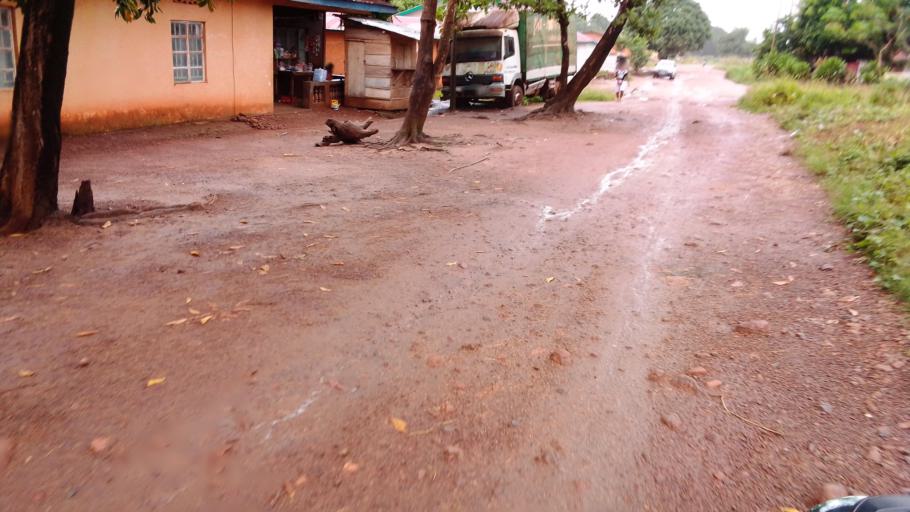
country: SL
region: Eastern Province
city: Kenema
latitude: 7.8994
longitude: -11.1805
